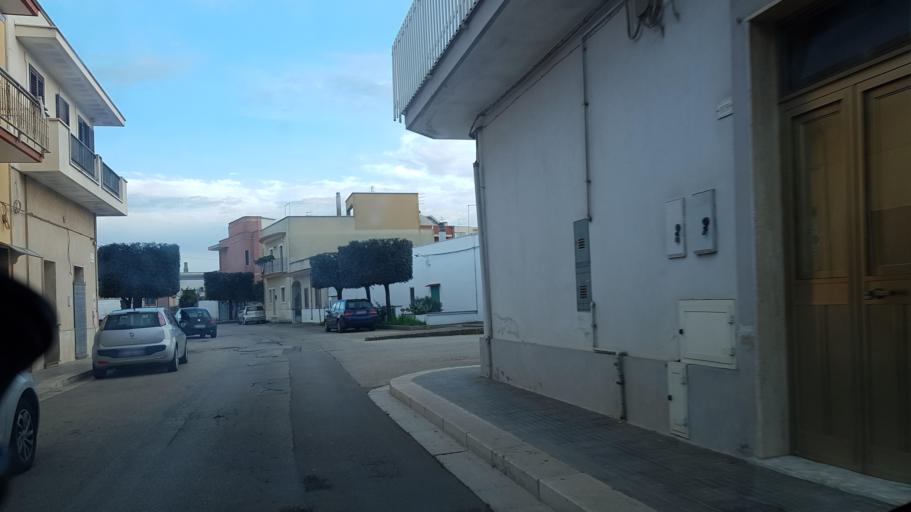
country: IT
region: Apulia
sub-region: Provincia di Brindisi
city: San Vito dei Normanni
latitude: 40.6535
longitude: 17.7002
